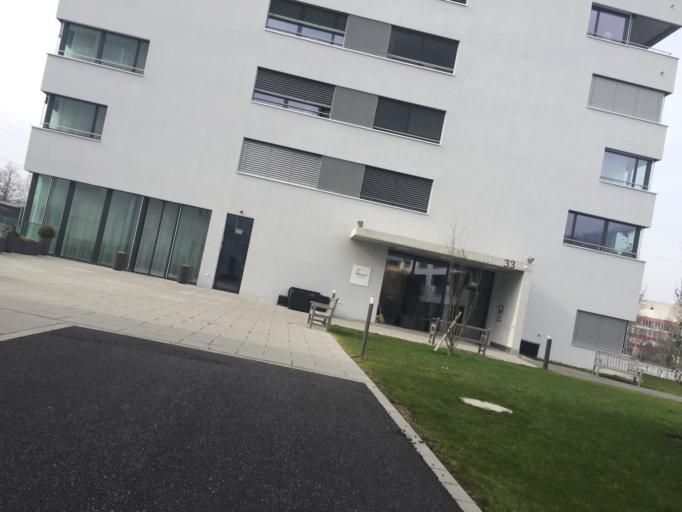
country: CH
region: Bern
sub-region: Thun District
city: Thun
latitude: 46.7611
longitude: 7.6206
